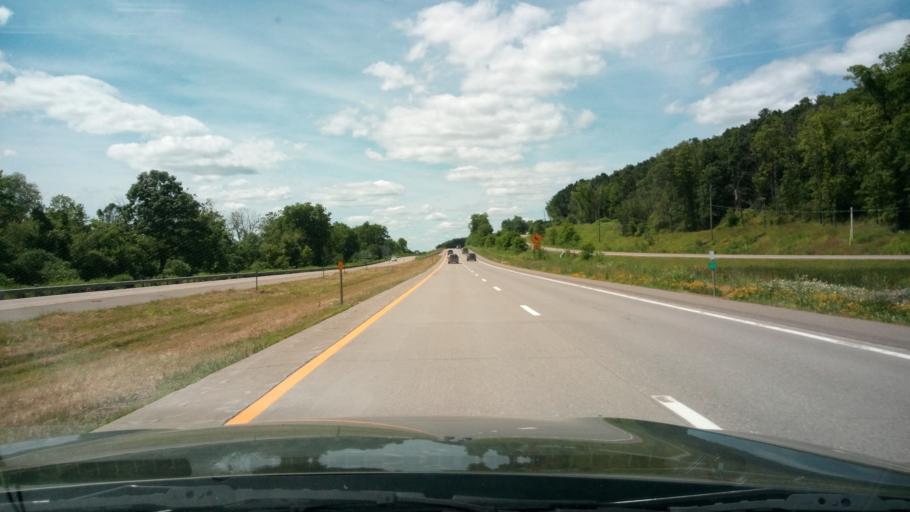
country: US
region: New York
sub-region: Chemung County
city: Southport
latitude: 42.0390
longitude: -76.7362
